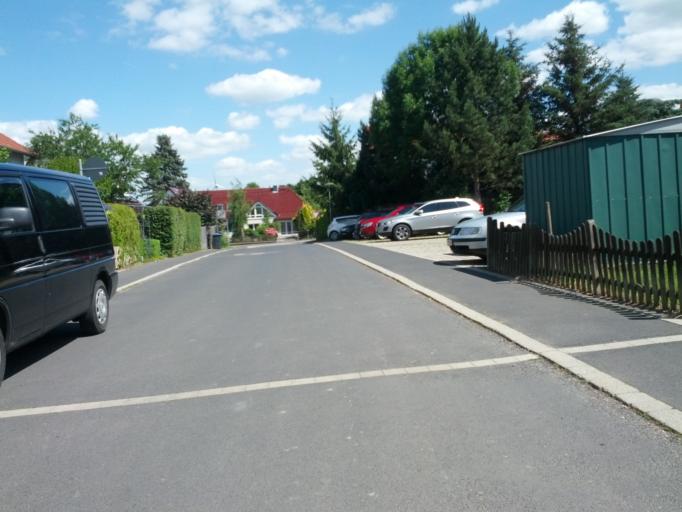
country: DE
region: Thuringia
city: Bischofroda
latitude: 51.0053
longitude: 10.3582
